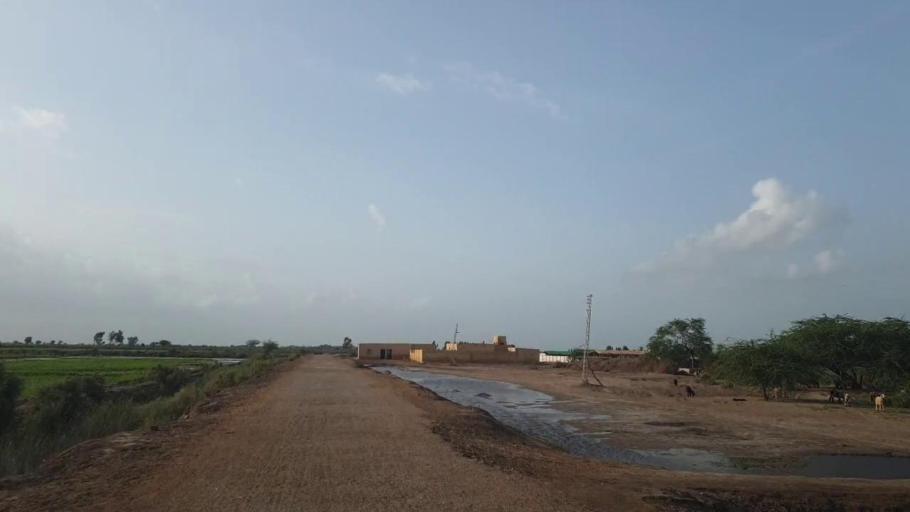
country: PK
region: Sindh
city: Tando Bago
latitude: 24.6608
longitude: 69.1120
